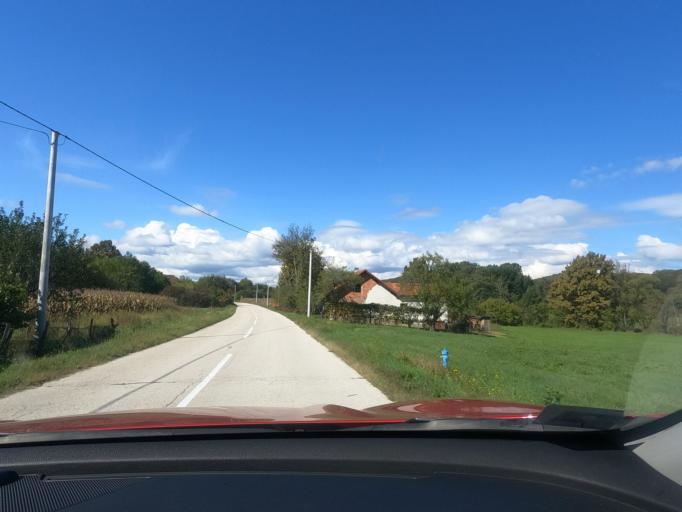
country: BA
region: Federation of Bosnia and Herzegovina
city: Vrnograc
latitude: 45.2334
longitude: 15.9264
